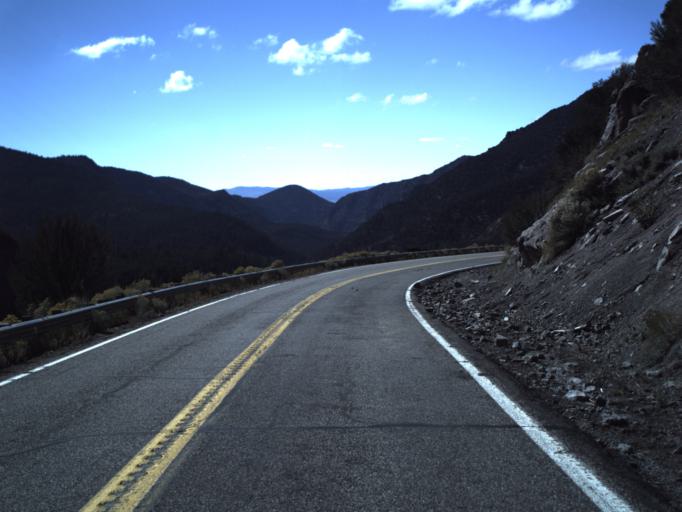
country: US
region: Utah
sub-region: Beaver County
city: Beaver
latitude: 38.2705
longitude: -112.4715
